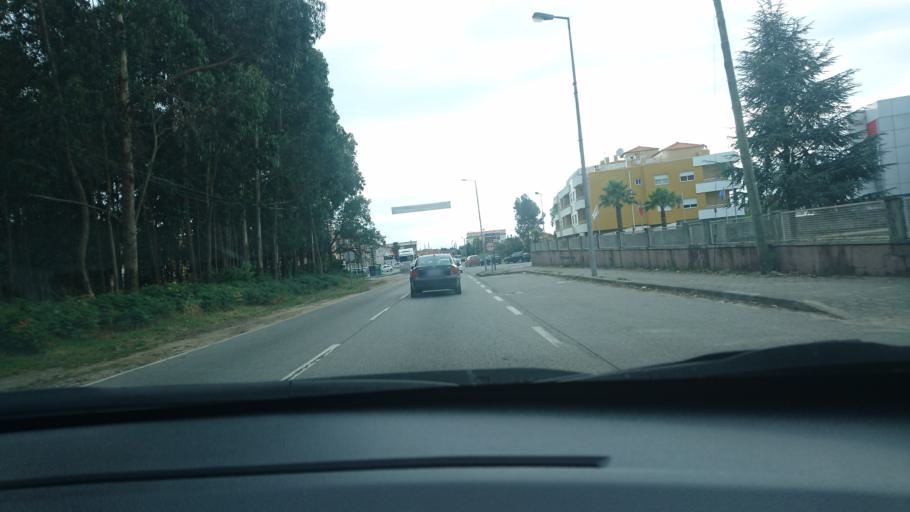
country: PT
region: Aveiro
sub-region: Santa Maria da Feira
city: Rio Meao
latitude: 40.9603
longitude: -8.5981
